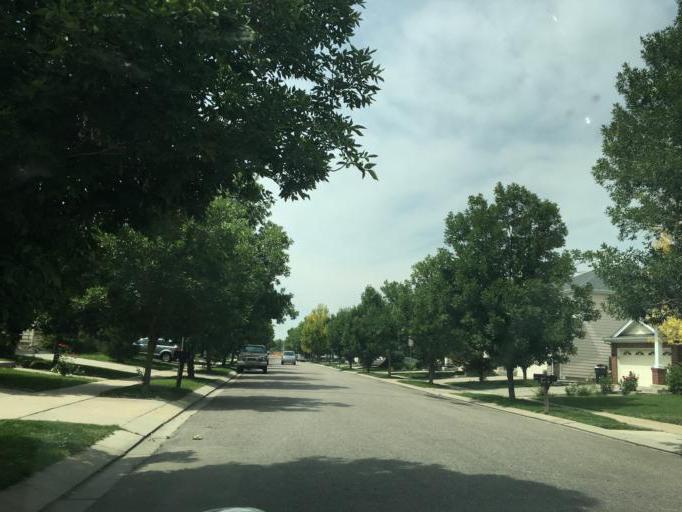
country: US
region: Colorado
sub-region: Adams County
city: Aurora
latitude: 39.7268
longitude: -104.8058
